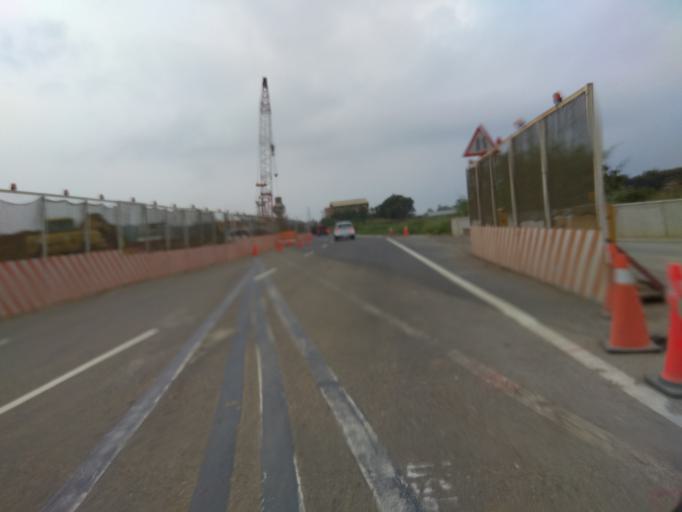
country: TW
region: Taiwan
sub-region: Hsinchu
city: Zhubei
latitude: 24.9001
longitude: 120.9701
